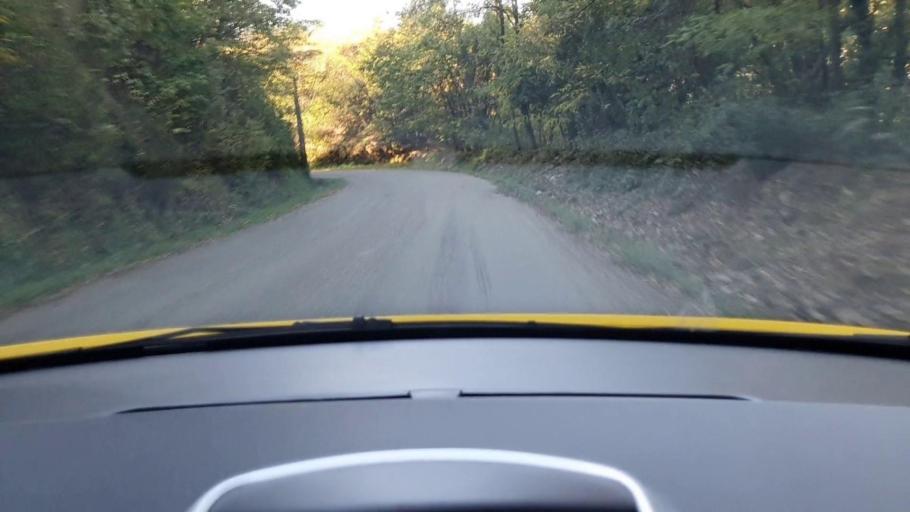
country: FR
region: Languedoc-Roussillon
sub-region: Departement du Gard
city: Sumene
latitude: 43.9911
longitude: 3.7519
